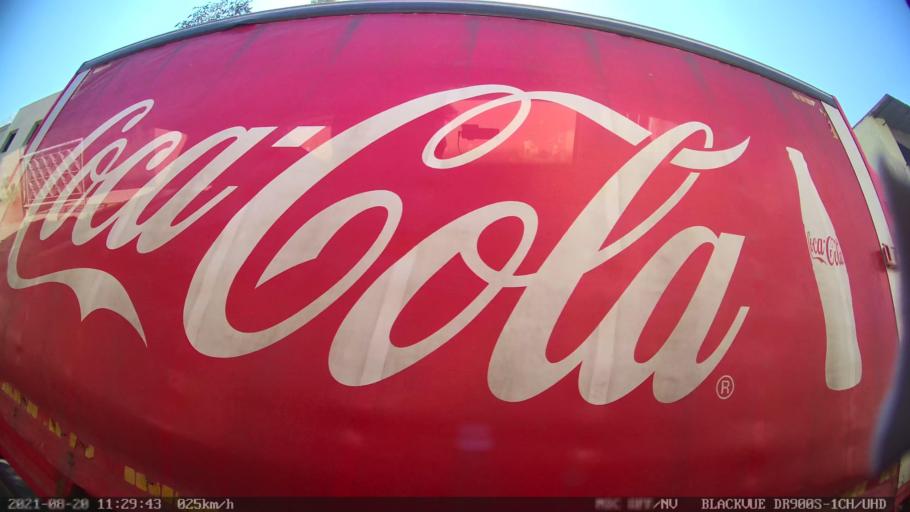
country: TR
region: Izmir
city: Karsiyaka
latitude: 38.4970
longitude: 27.0670
